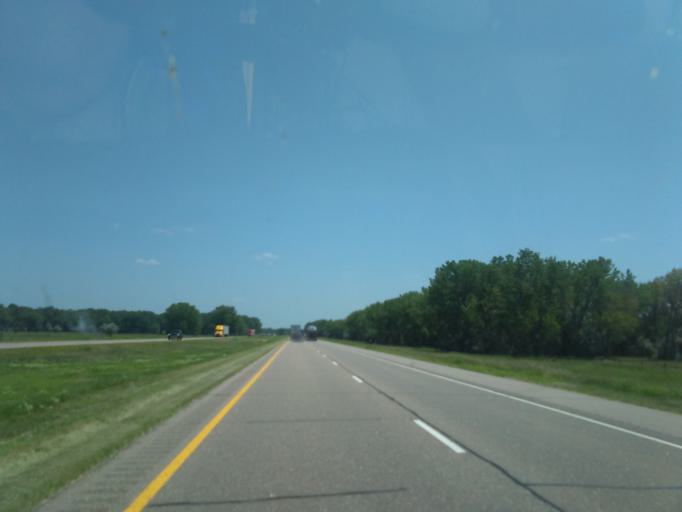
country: US
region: Nebraska
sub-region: Dawson County
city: Gothenburg
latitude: 40.8918
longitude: -100.1102
